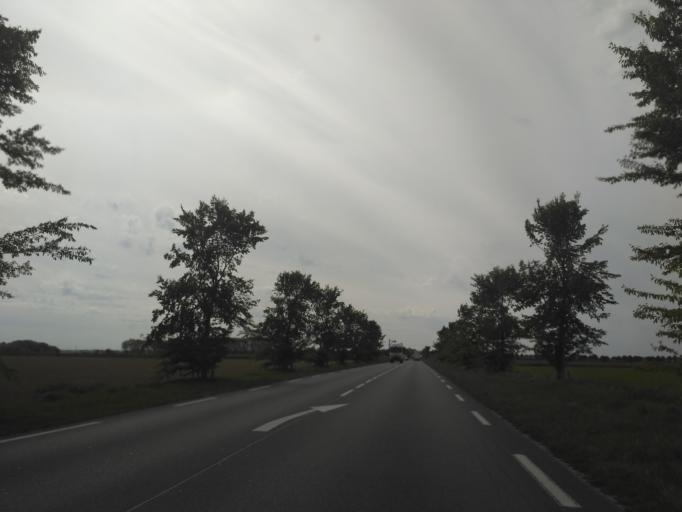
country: FR
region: Ile-de-France
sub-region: Departement de Seine-et-Marne
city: Moissy-Cramayel
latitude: 48.6314
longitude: 2.6441
